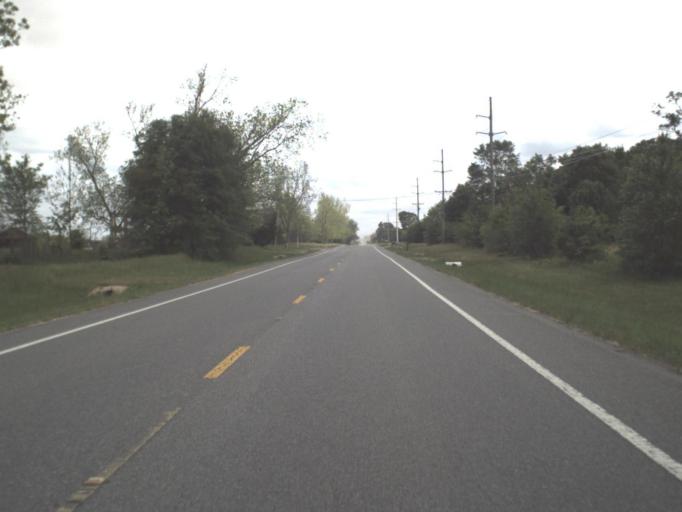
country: US
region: Florida
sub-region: Santa Rosa County
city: Point Baker
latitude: 30.7971
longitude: -87.0922
